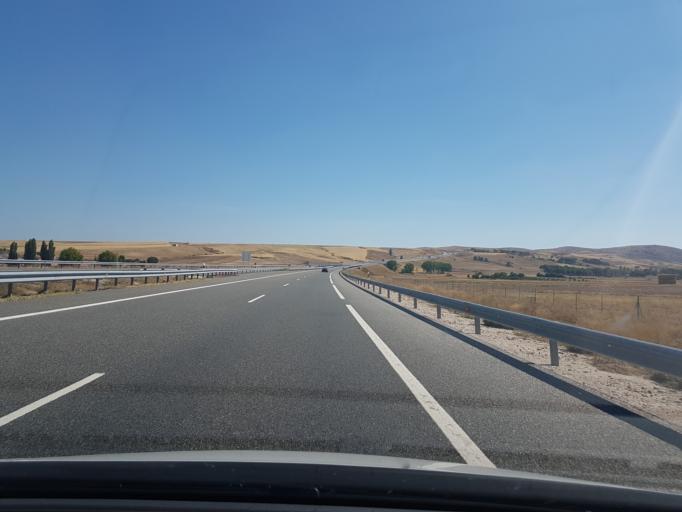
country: ES
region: Castille and Leon
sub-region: Provincia de Avila
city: Monsalupe
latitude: 40.7951
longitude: -4.7739
